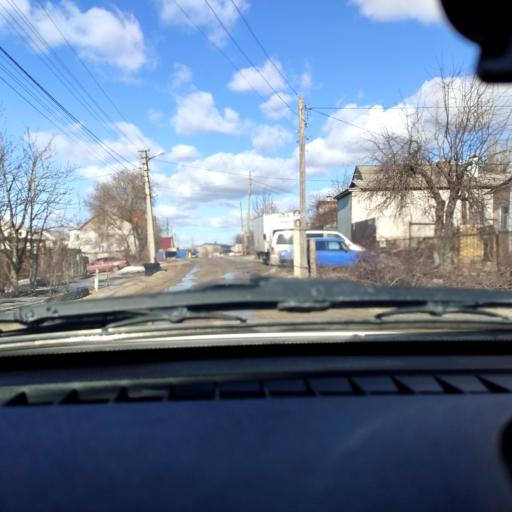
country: RU
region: Voronezj
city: Pridonskoy
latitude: 51.6892
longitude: 39.0578
